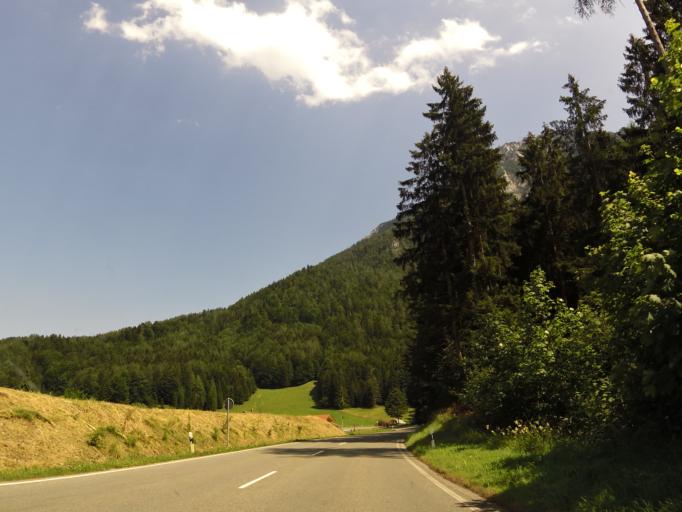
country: DE
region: Bavaria
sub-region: Upper Bavaria
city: Ruhpolding
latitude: 47.7418
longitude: 12.6651
